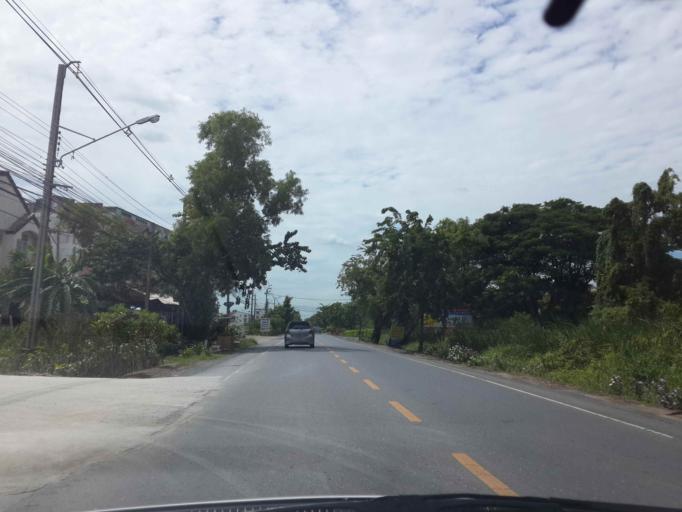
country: TH
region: Bangkok
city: Khan Na Yao
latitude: 13.8655
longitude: 100.6920
